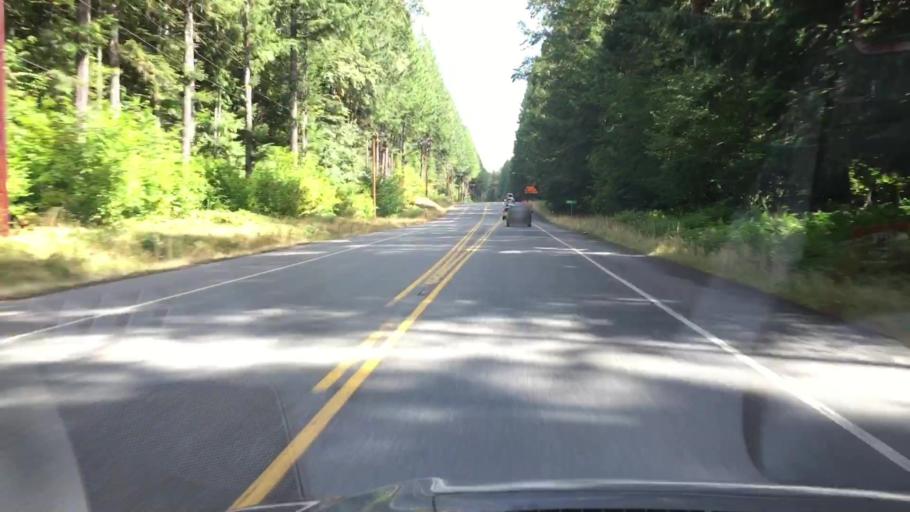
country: US
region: Washington
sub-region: Pierce County
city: Eatonville
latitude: 46.7548
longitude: -122.1229
